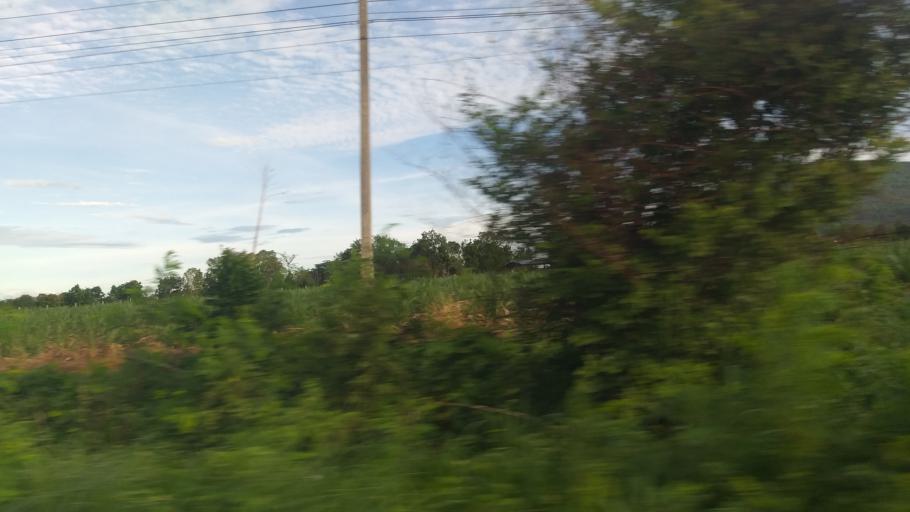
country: TH
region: Chaiyaphum
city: Ban Thaen
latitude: 16.3537
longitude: 102.2454
